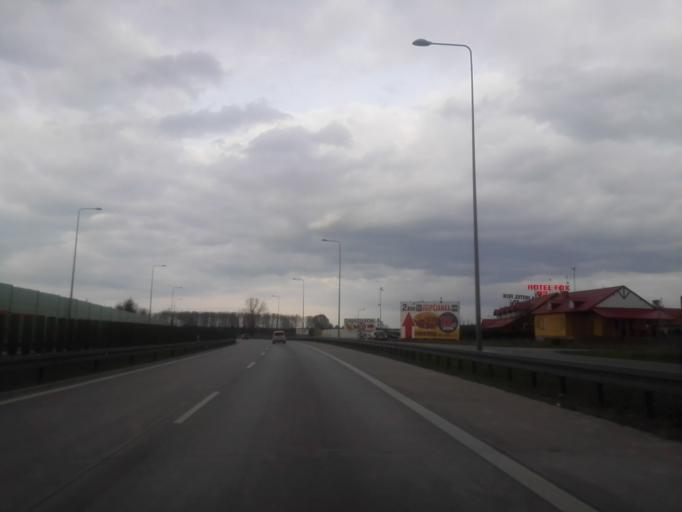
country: PL
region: Lodz Voivodeship
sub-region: Powiat piotrkowski
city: Wolborz
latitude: 51.5060
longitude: 19.8853
